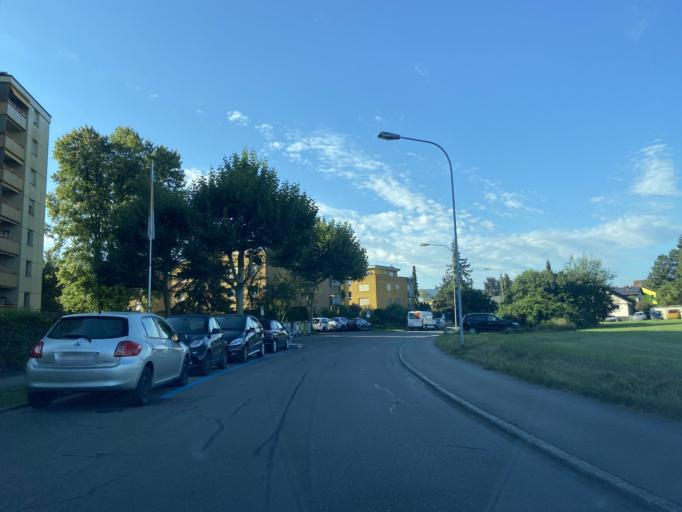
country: CH
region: Zurich
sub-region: Bezirk Buelach
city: Dietlikon / Eichwiesen
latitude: 47.4181
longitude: 8.6213
